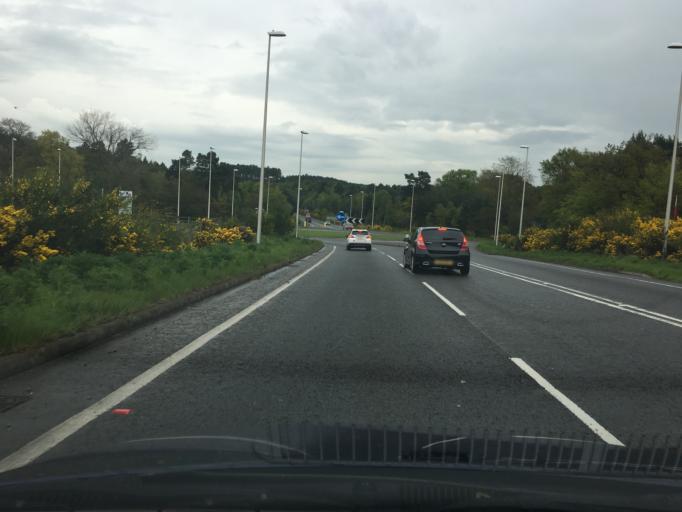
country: GB
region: England
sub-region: Bracknell Forest
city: Crowthorne
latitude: 51.3669
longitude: -0.7662
